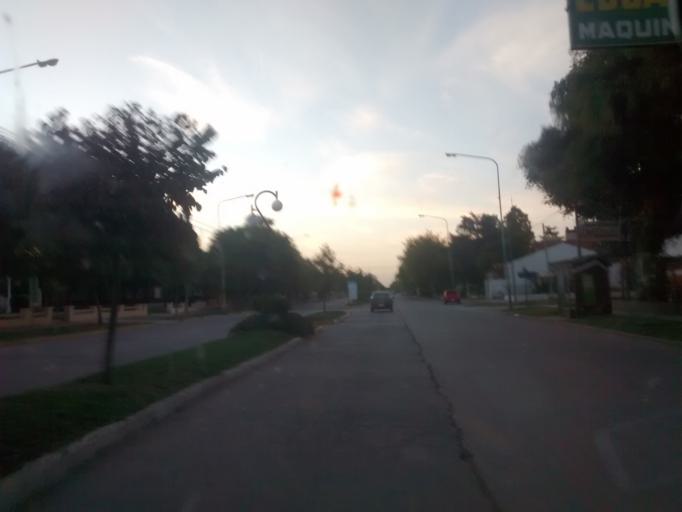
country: AR
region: Buenos Aires
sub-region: Partido de Loberia
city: Loberia
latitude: -38.1718
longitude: -58.7722
